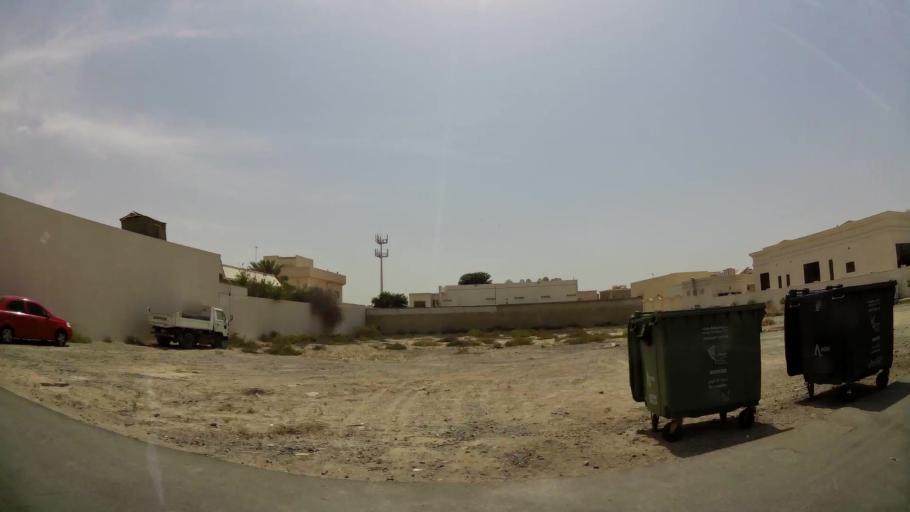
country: AE
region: Ash Shariqah
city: Sharjah
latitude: 25.2446
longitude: 55.4226
